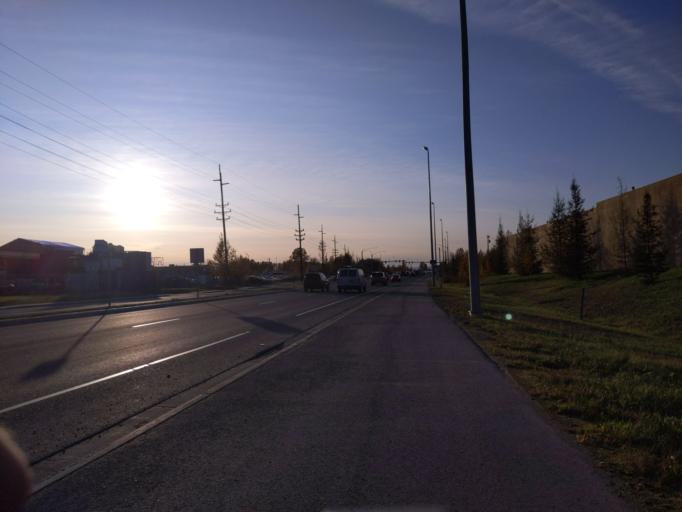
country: US
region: Alaska
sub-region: Anchorage Municipality
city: Anchorage
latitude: 61.1666
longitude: -149.8811
